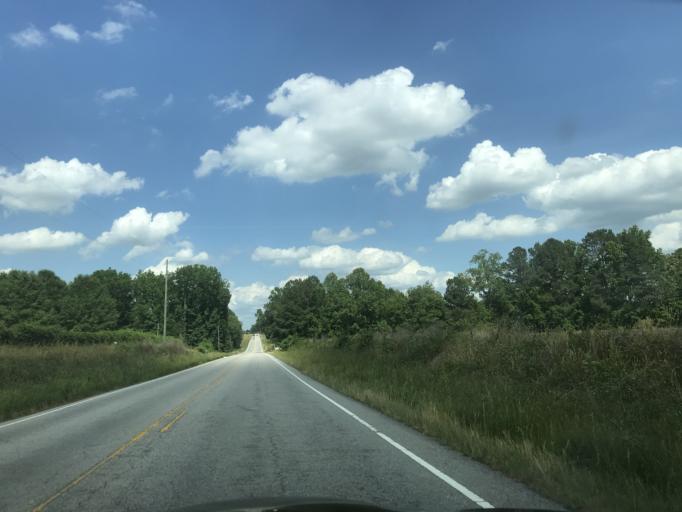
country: US
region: North Carolina
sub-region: Wake County
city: Rolesville
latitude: 35.9663
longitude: -78.4131
